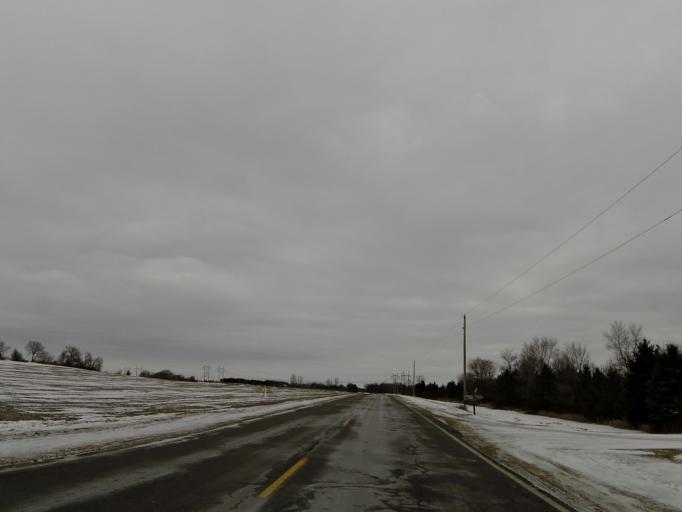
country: US
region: Minnesota
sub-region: Washington County
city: Cottage Grove
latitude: 44.8263
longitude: -92.8903
